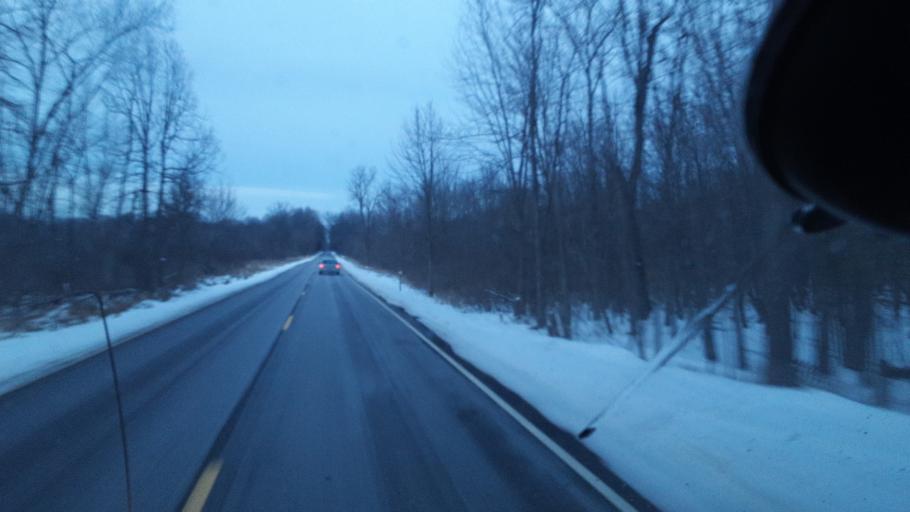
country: US
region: Michigan
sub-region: Jackson County
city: Grass Lake
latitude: 42.3474
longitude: -84.2099
